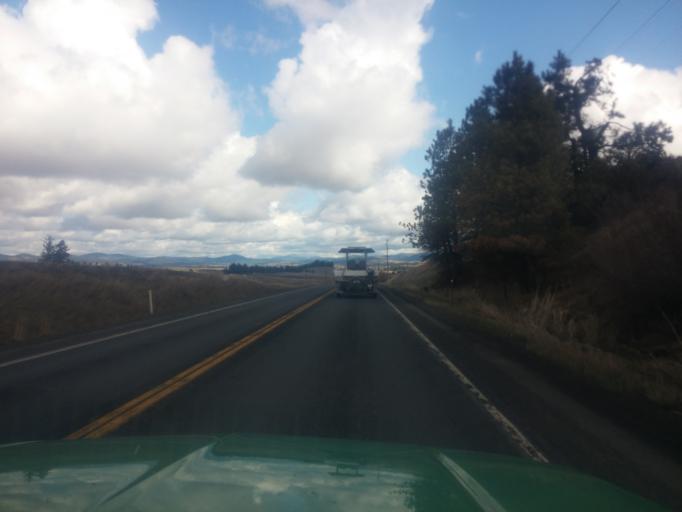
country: US
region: Idaho
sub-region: Latah County
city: Moscow
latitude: 46.8875
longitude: -116.9994
